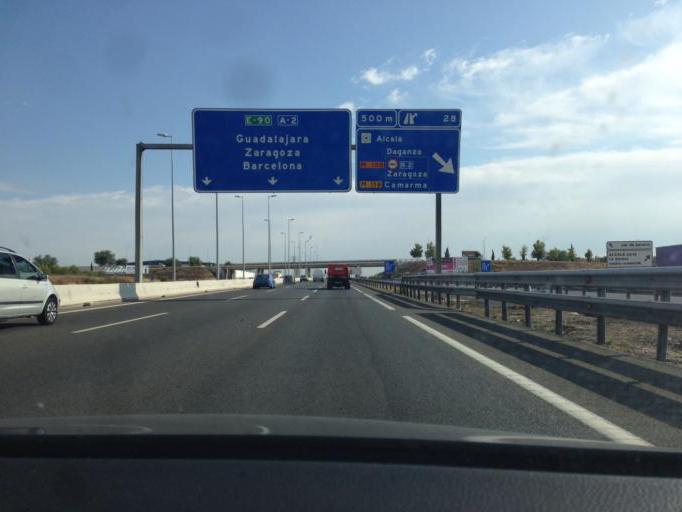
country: ES
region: Madrid
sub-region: Provincia de Madrid
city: Alcala de Henares
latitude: 40.4817
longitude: -3.4016
